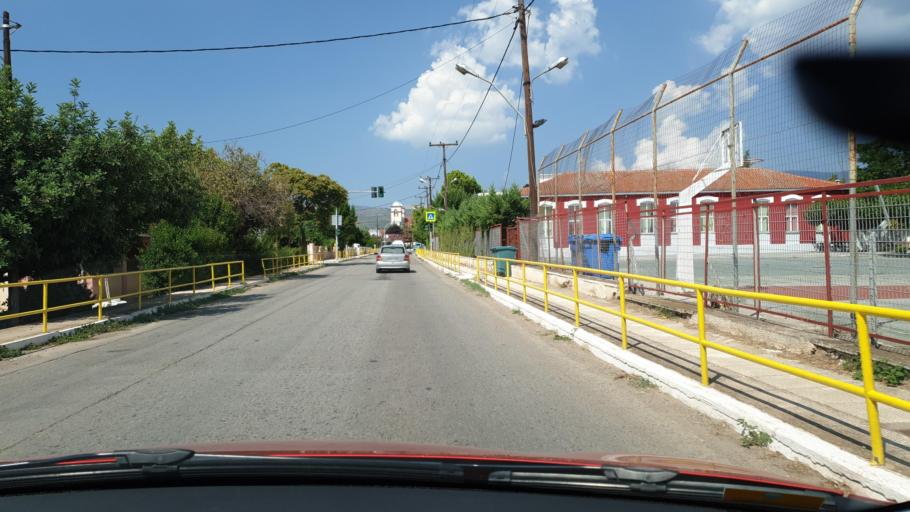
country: GR
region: Central Greece
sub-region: Nomos Evvoias
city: Kastella
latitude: 38.5681
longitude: 23.6307
